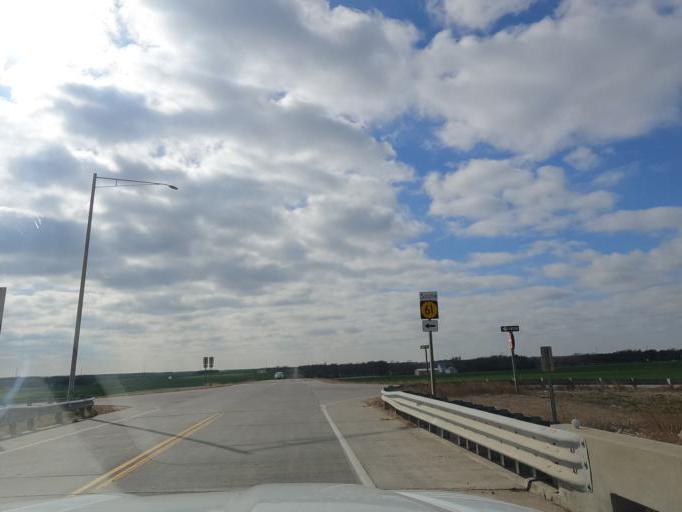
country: US
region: Kansas
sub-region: McPherson County
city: Inman
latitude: 38.2317
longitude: -97.7850
